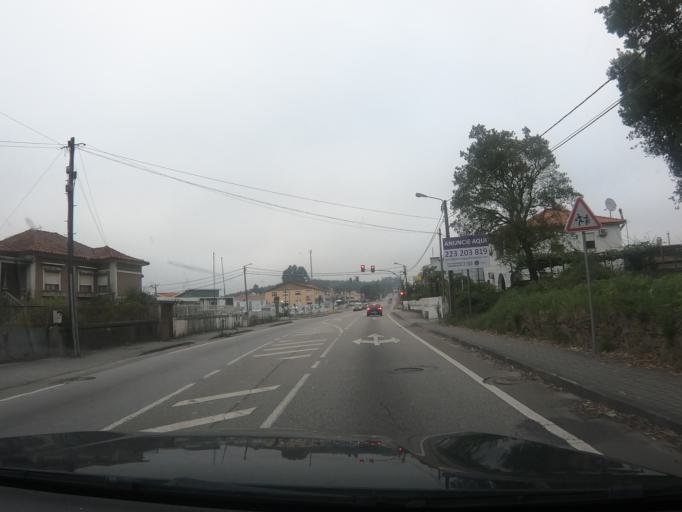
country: PT
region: Aveiro
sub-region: Santa Maria da Feira
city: Argoncilhe
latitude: 41.0122
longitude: -8.5562
